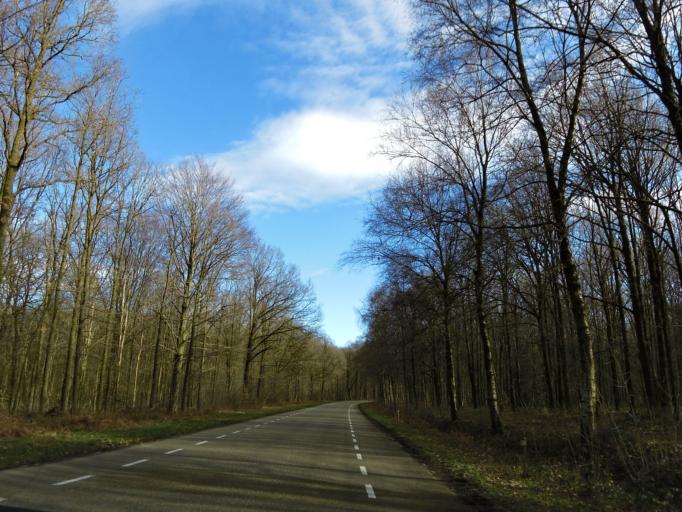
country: BE
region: Wallonia
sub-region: Province de Liege
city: Plombieres
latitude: 50.7671
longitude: 5.9573
